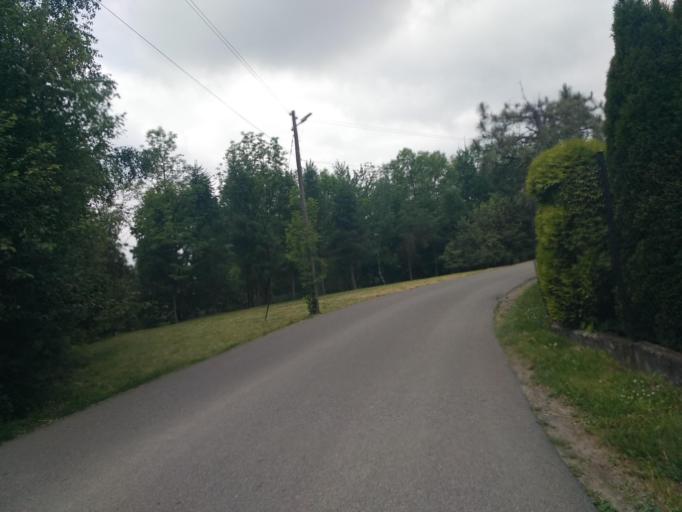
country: PL
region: Subcarpathian Voivodeship
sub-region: Powiat krosnienski
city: Chorkowka
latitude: 49.6701
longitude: 21.6973
